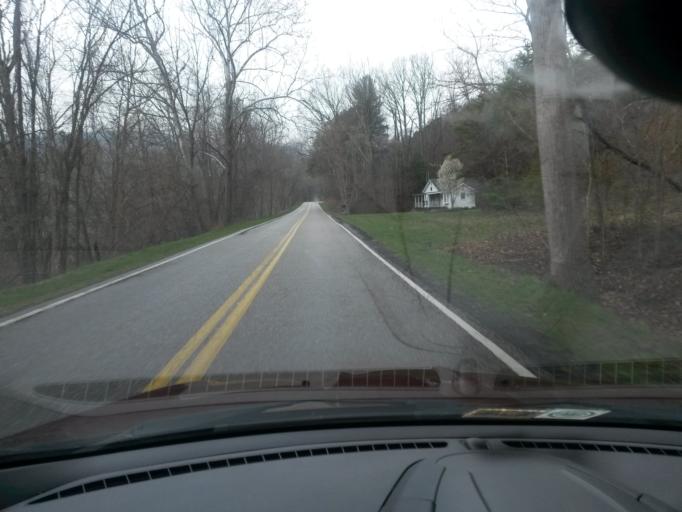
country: US
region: Virginia
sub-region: Alleghany County
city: Clifton Forge
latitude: 37.9010
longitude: -79.7401
